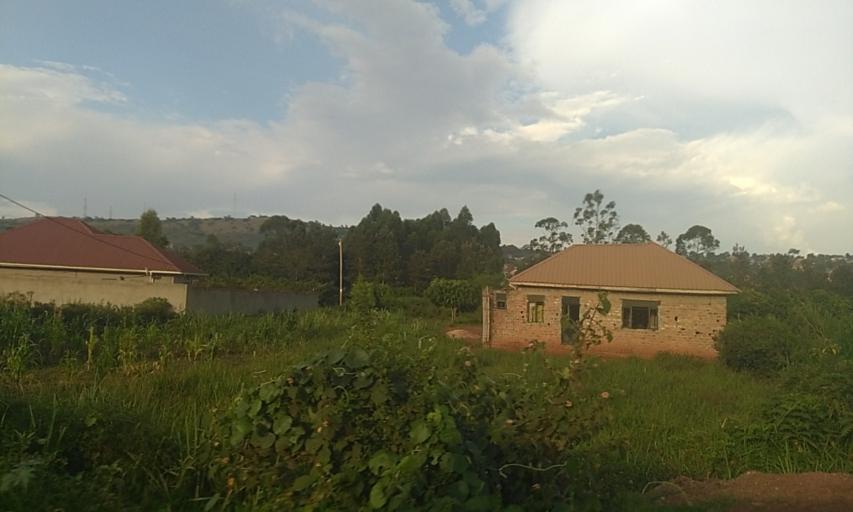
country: UG
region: Central Region
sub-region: Wakiso District
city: Kajansi
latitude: 0.2677
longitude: 32.5277
